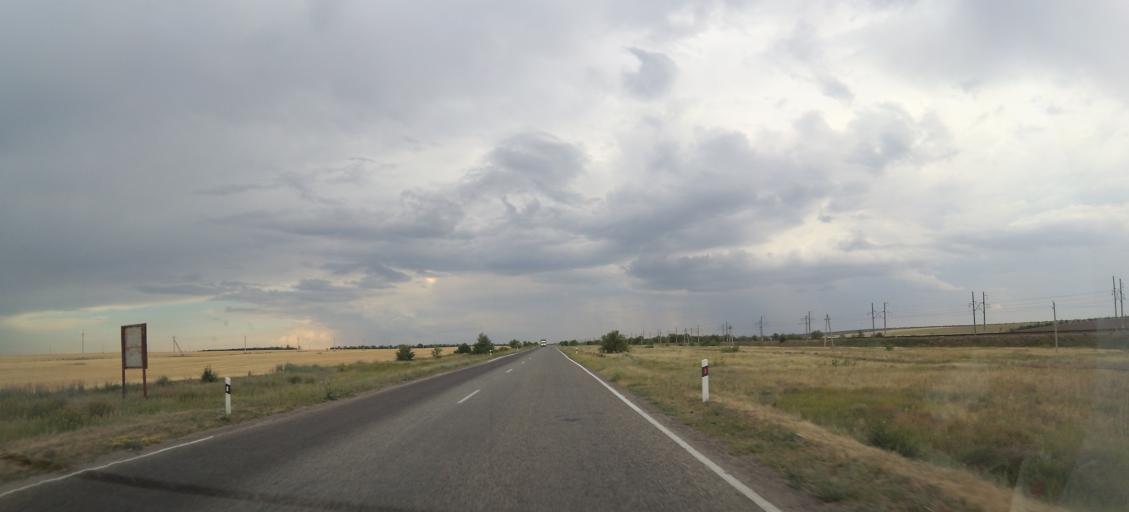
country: RU
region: Rostov
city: Dubovskoye
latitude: 47.4358
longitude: 42.7913
